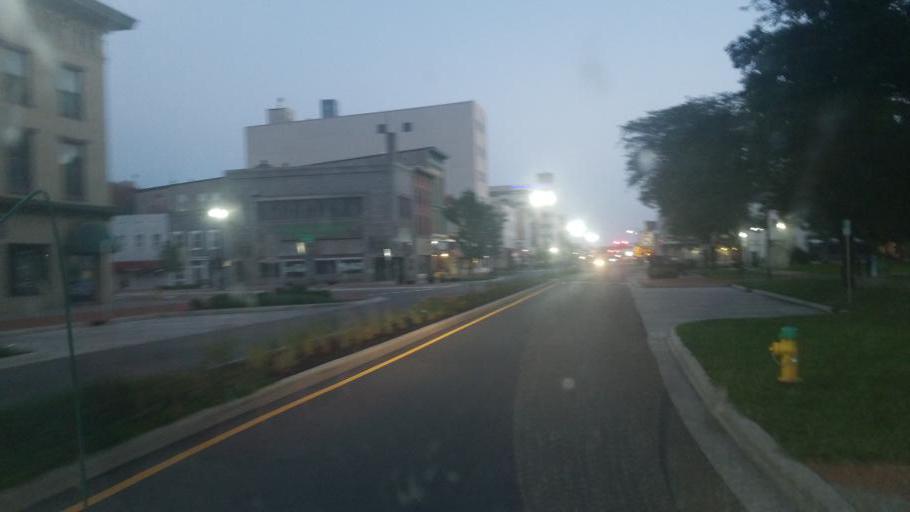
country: US
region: Ohio
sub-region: Licking County
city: Newark
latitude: 40.0573
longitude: -82.4023
